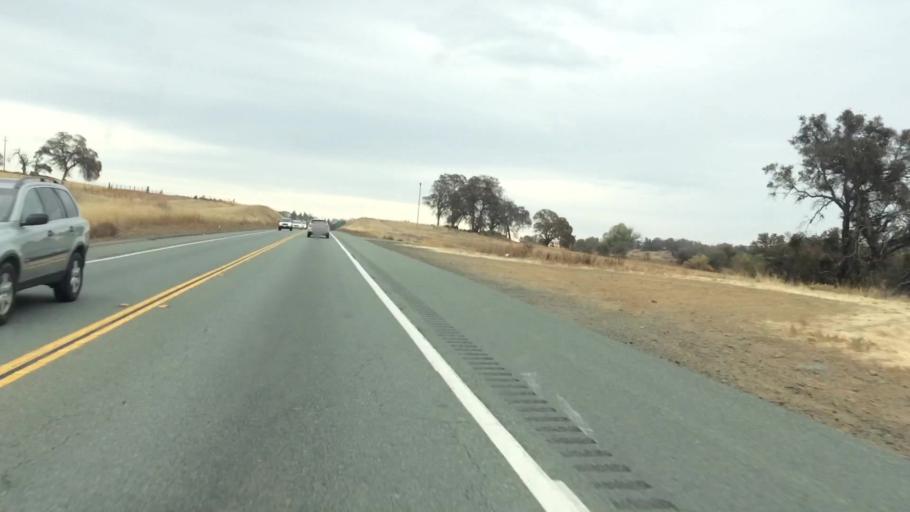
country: US
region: California
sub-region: Amador County
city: Sutter Creek
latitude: 38.3872
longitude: -120.8135
